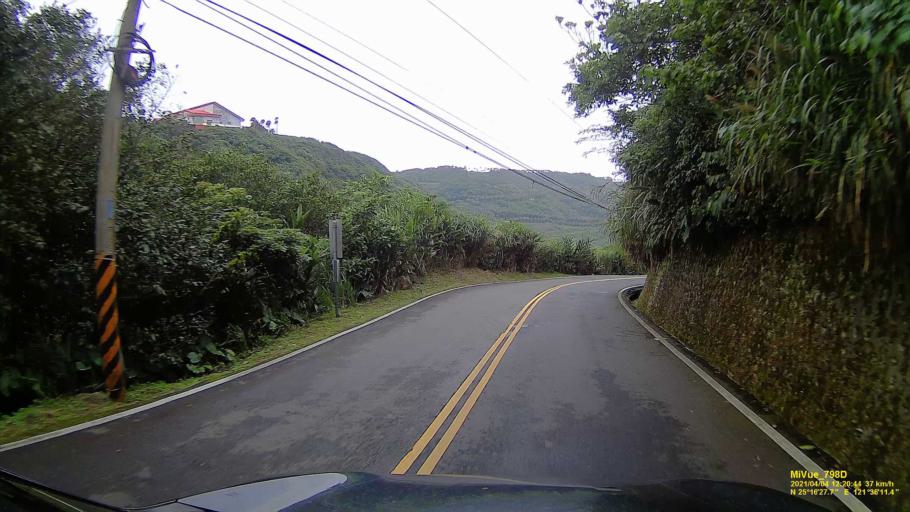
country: TW
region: Taiwan
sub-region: Keelung
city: Keelung
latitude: 25.2746
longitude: 121.6032
